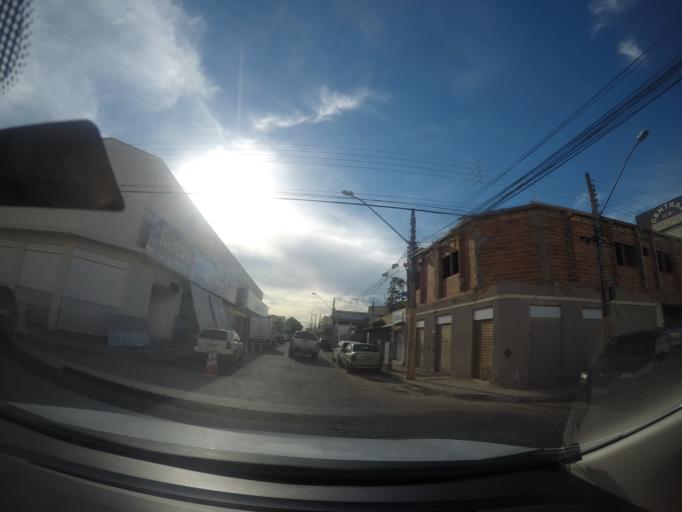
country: BR
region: Goias
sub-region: Goiania
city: Goiania
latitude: -16.6734
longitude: -49.2892
